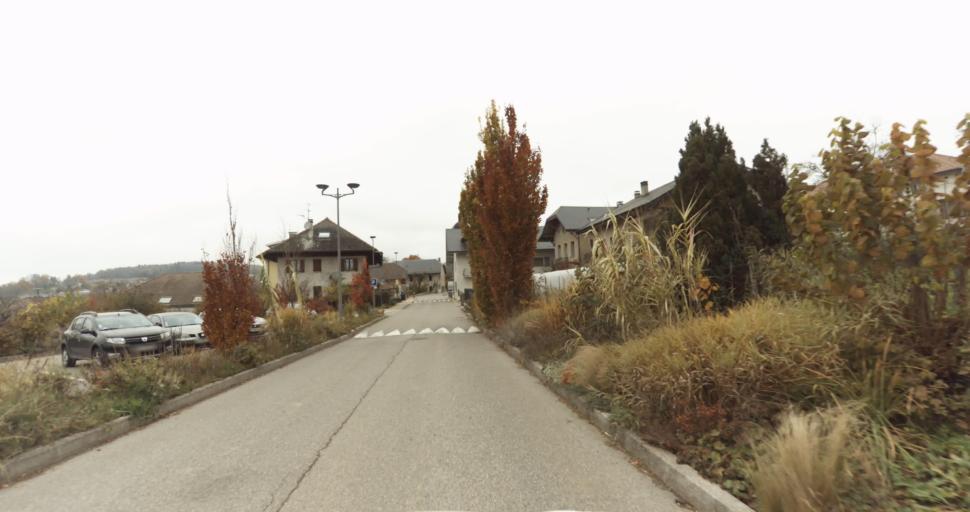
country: FR
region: Rhone-Alpes
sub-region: Departement de la Haute-Savoie
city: Alby-sur-Cheran
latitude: 45.8443
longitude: 6.0375
